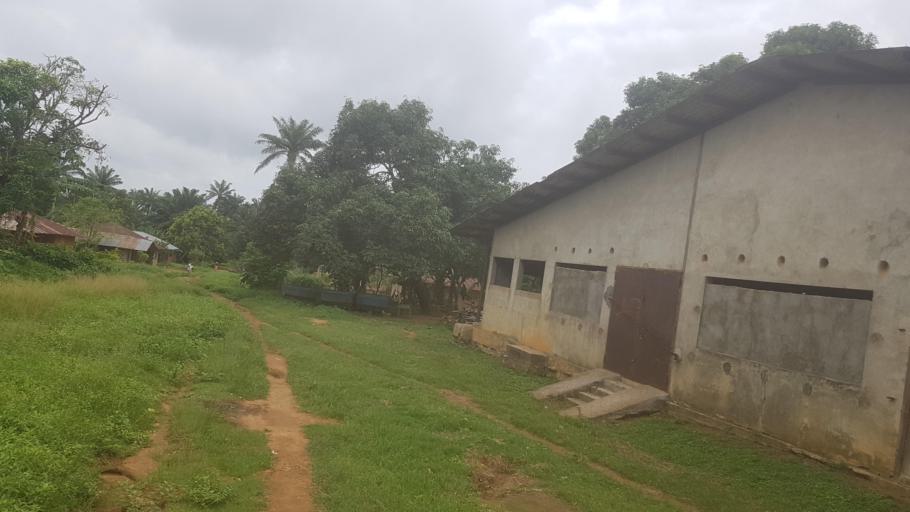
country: SL
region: Southern Province
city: Sumbuya
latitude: 7.5345
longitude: -12.1778
